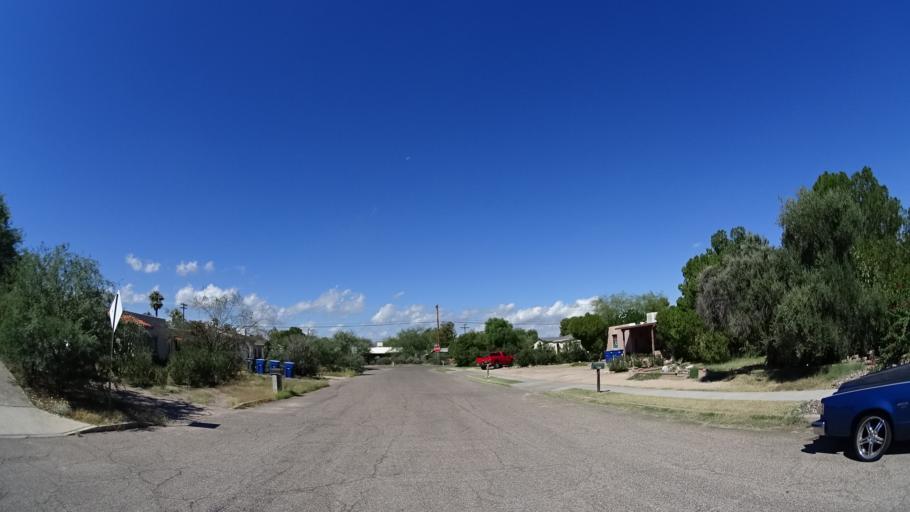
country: US
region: Arizona
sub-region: Pima County
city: Tucson
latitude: 32.2557
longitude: -110.9560
